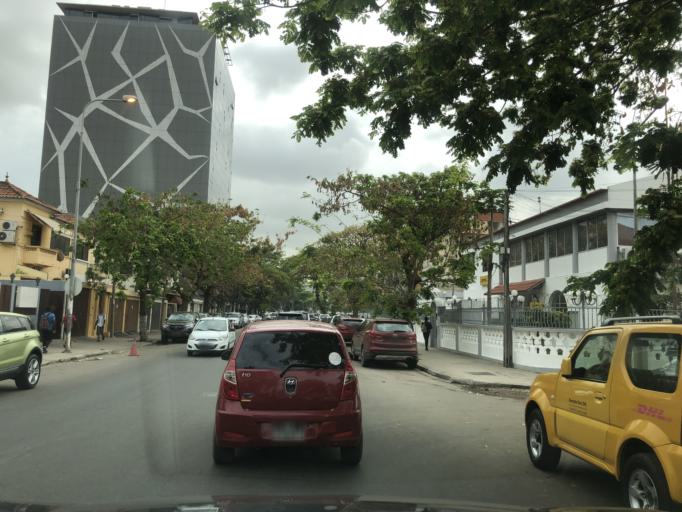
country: AO
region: Luanda
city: Luanda
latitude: -8.8256
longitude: 13.2366
